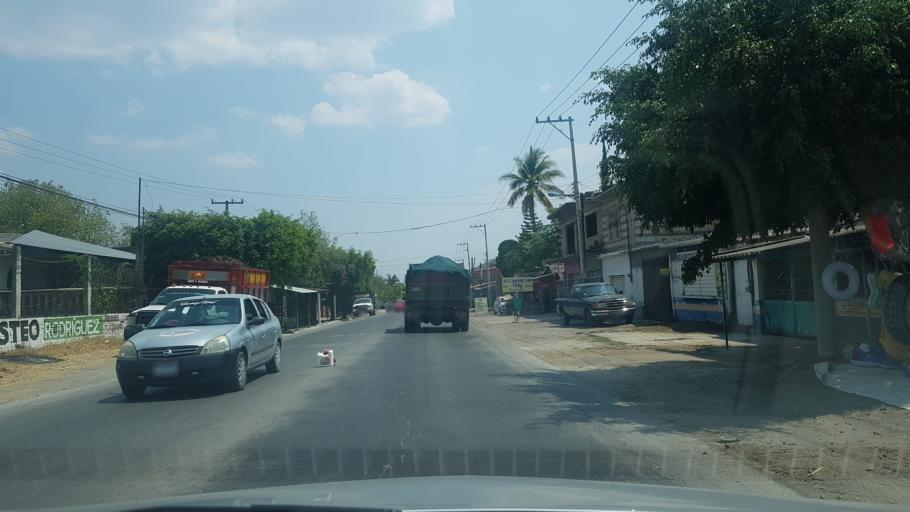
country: MX
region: Morelos
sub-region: Tlaltizapan de Zapata
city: Colonia Palo Prieto (Chipitongo)
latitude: 18.7202
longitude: -99.1208
